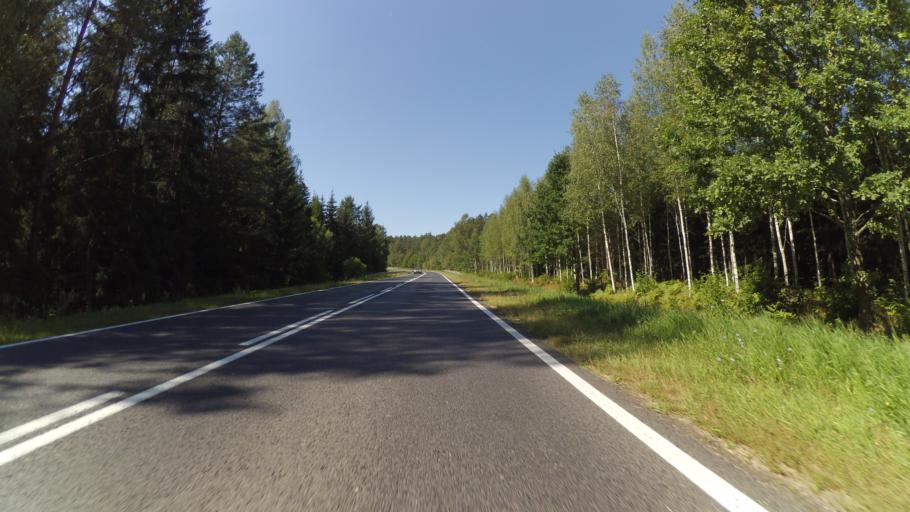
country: PL
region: Podlasie
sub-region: Powiat bialostocki
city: Michalowo
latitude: 53.1439
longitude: 23.4981
